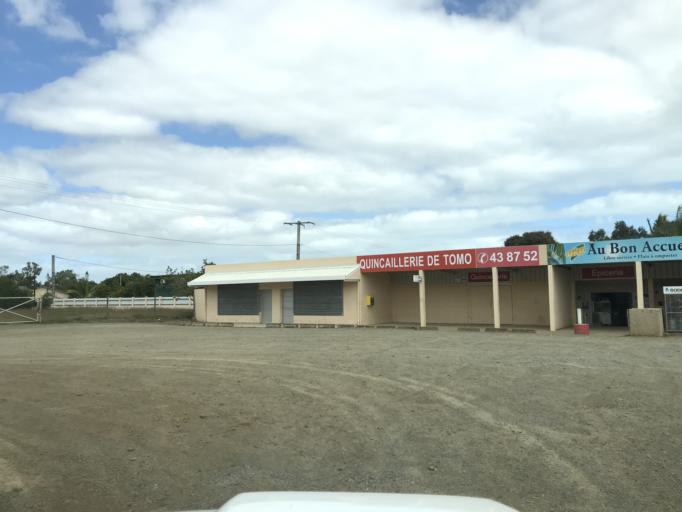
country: NC
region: South Province
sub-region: Bouloupari
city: Bouloupari
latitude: -21.9569
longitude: 166.1461
